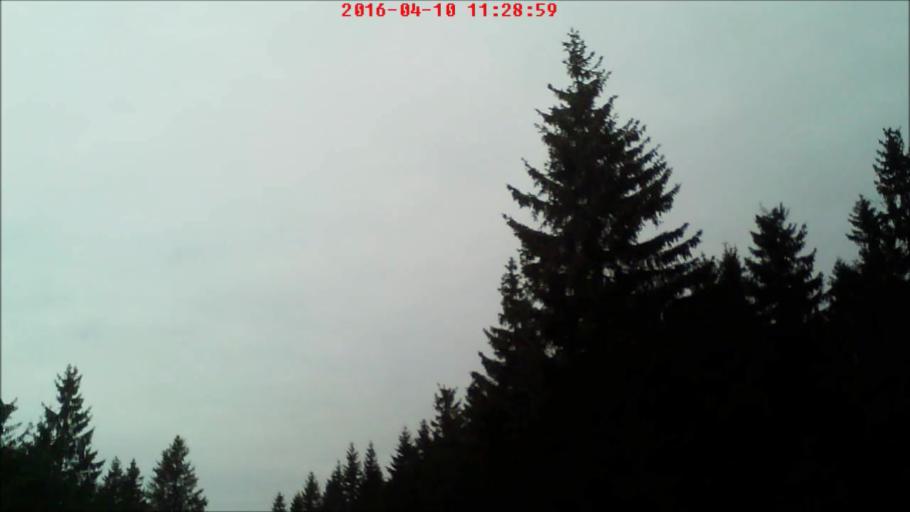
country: DE
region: Thuringia
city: Gehlberg
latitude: 50.6548
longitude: 10.7700
